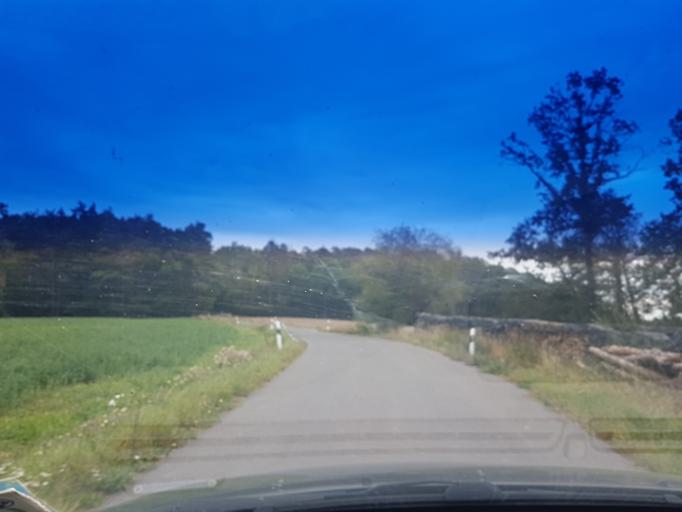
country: DE
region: Bavaria
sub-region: Regierungsbezirk Unterfranken
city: Geiselwind
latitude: 49.8223
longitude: 10.4932
